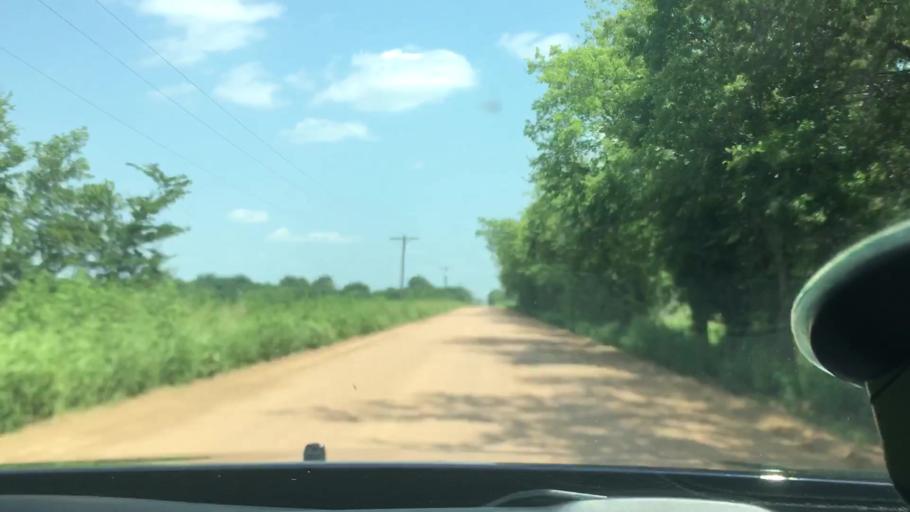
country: US
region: Oklahoma
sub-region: Johnston County
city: Tishomingo
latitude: 34.4196
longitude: -96.4857
